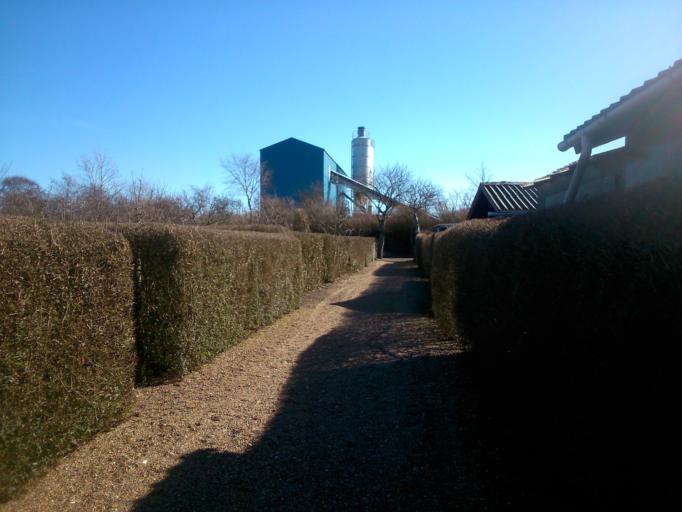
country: DK
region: Central Jutland
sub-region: Ringkobing-Skjern Kommune
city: Ringkobing
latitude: 56.0894
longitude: 8.2562
